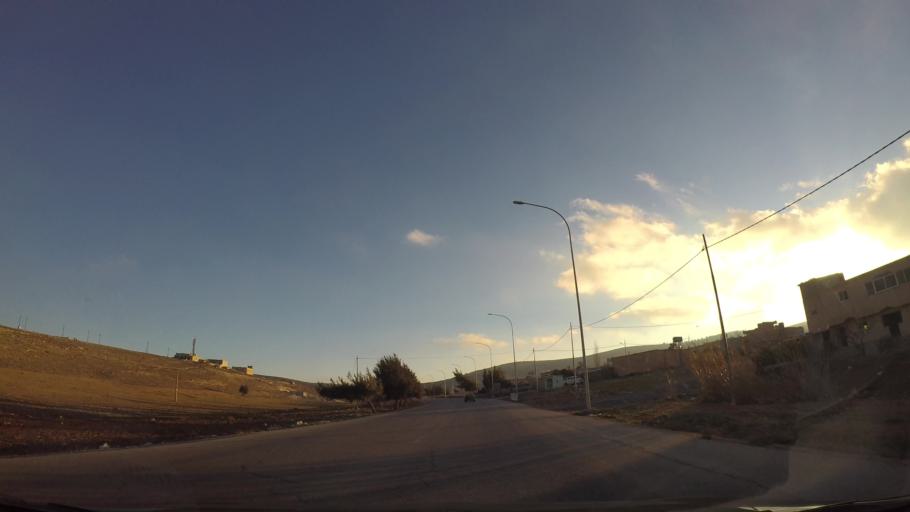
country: JO
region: Ma'an
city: Petra
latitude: 30.4411
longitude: 35.5193
